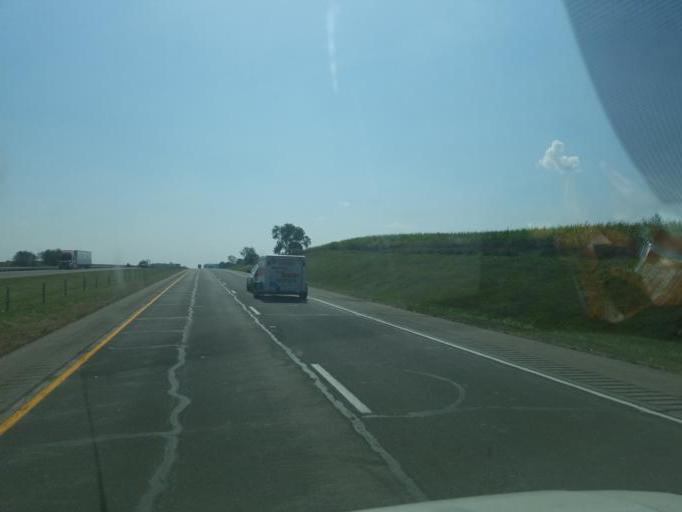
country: US
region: Indiana
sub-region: Steuben County
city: Angola
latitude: 41.5690
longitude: -85.0580
